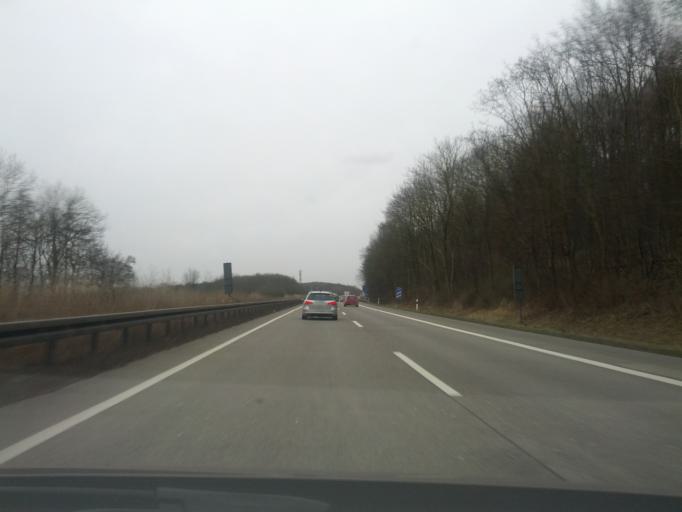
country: DE
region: Lower Saxony
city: Bad Salzdetfurth
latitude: 52.1309
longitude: 10.0411
